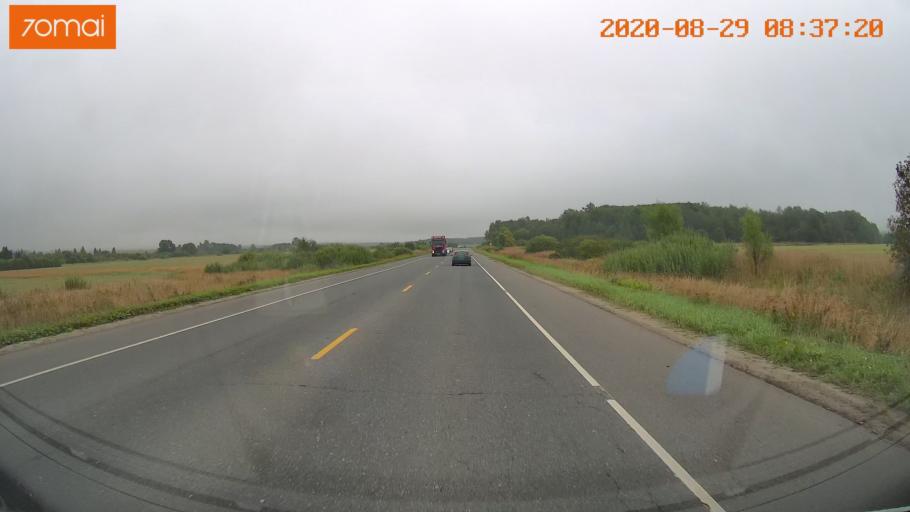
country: RU
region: Ivanovo
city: Rodniki
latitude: 57.0878
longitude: 41.6438
